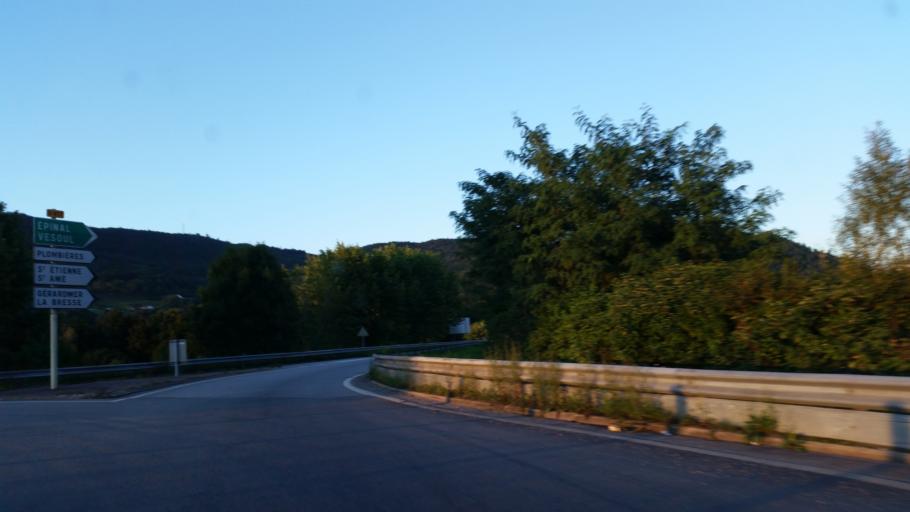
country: FR
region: Lorraine
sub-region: Departement des Vosges
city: Saint-Etienne-les-Remiremont
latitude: 48.0143
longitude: 6.6078
